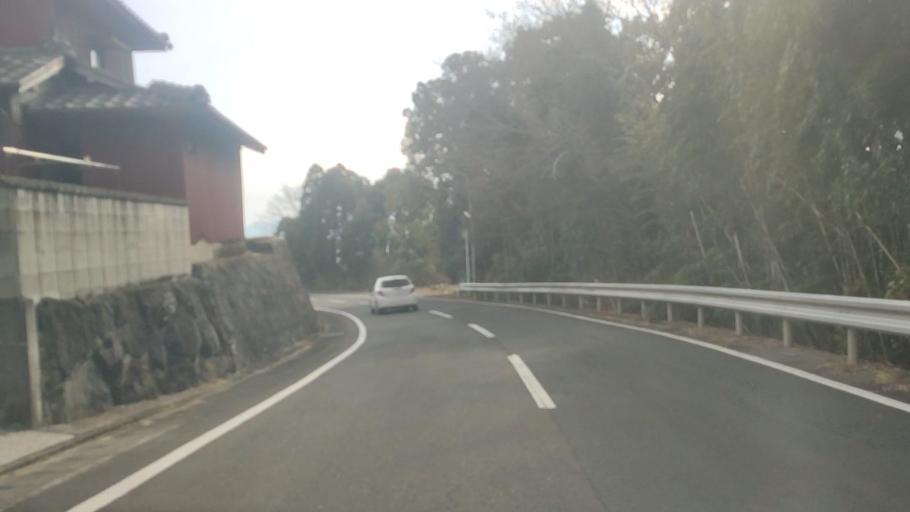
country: JP
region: Nagasaki
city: Shimabara
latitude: 32.6737
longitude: 130.2818
